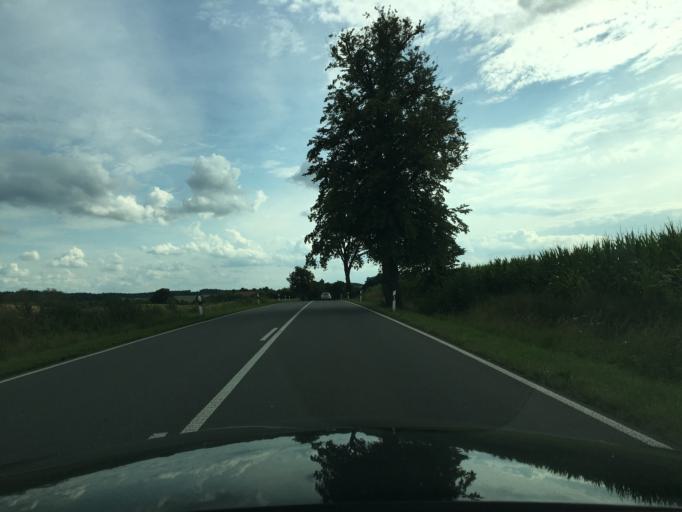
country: DE
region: Mecklenburg-Vorpommern
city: Penzlin
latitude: 53.4556
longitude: 13.0576
